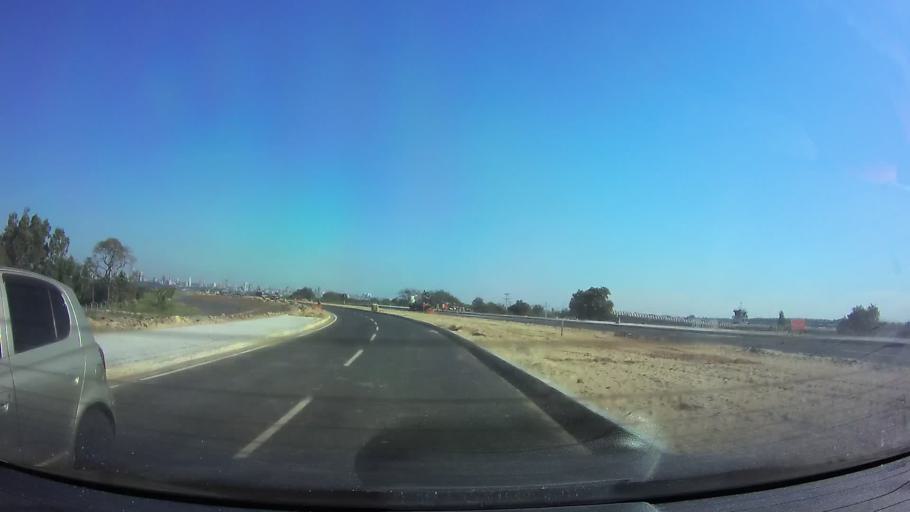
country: PY
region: Asuncion
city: Asuncion
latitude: -25.2498
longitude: -57.6033
